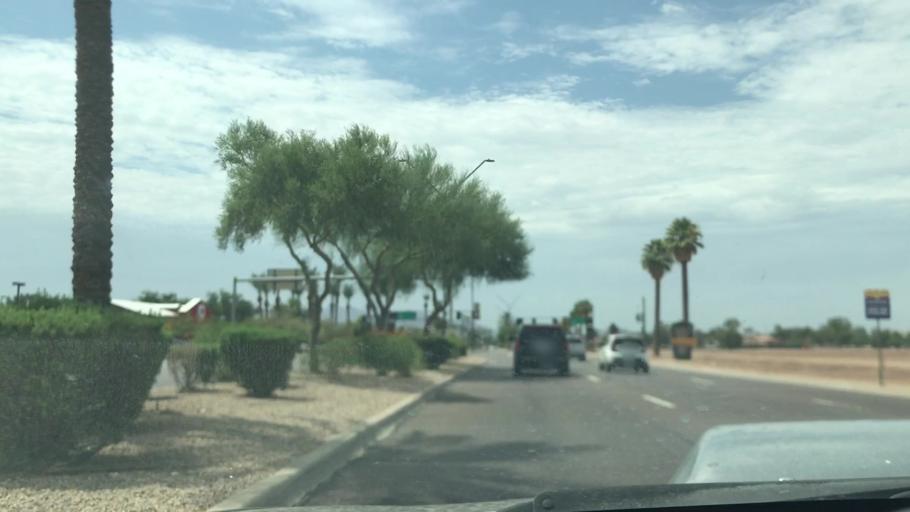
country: US
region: Arizona
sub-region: Maricopa County
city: Goodyear
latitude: 33.4567
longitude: -112.3582
